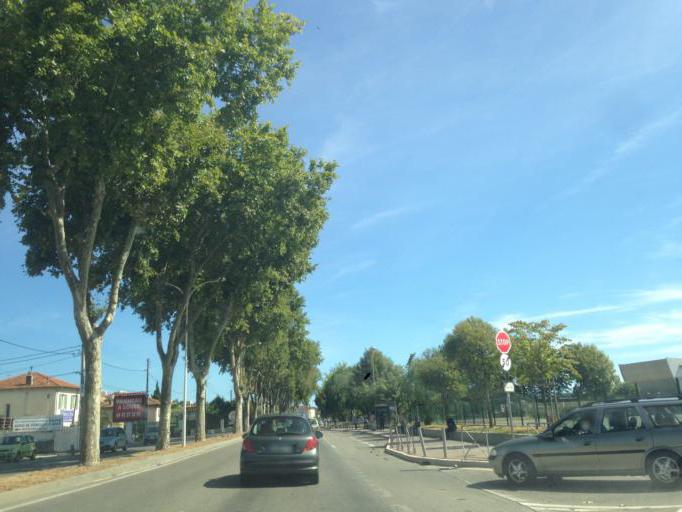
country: FR
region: Provence-Alpes-Cote d'Azur
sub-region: Departement des Alpes-Maritimes
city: Saint-Laurent-du-Var
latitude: 43.6935
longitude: 7.1938
